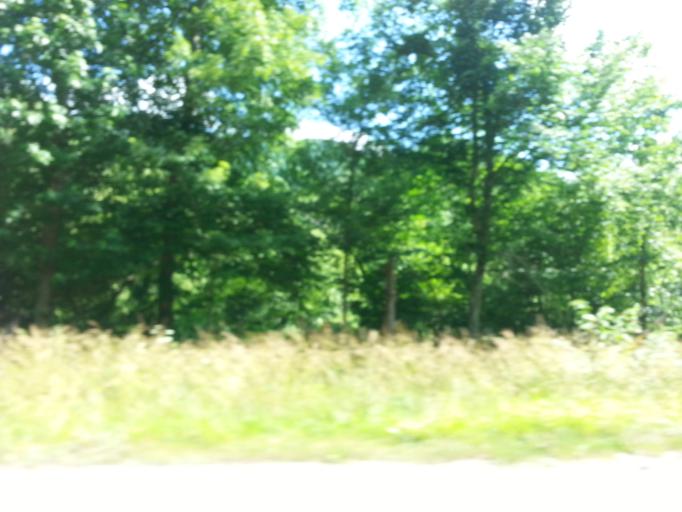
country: US
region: Kentucky
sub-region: Harlan County
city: Cumberland
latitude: 36.9473
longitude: -83.1077
